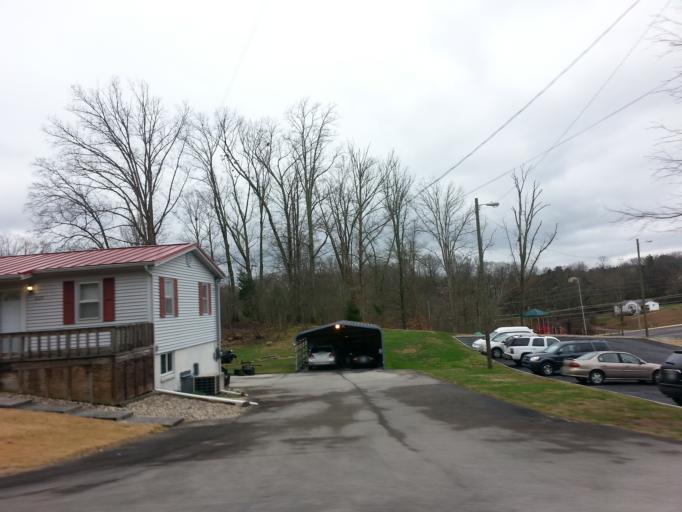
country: US
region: Tennessee
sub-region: Knox County
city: Knoxville
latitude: 35.9858
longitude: -84.0274
